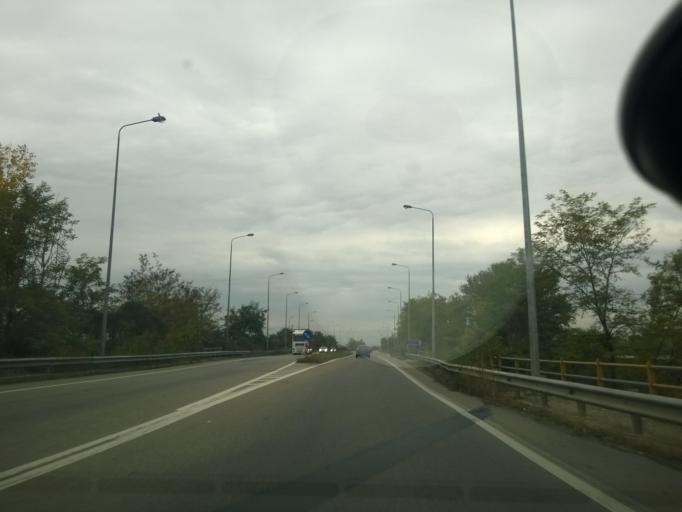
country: GR
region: Central Macedonia
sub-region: Nomos Pellis
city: Karyotissa
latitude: 40.7785
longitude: 22.3168
